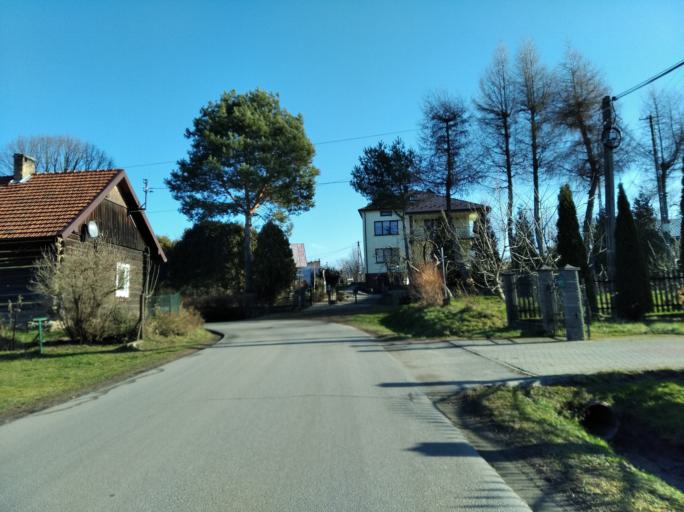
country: PL
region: Subcarpathian Voivodeship
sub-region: Powiat strzyzowski
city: Jawornik
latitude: 49.8024
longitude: 21.8818
